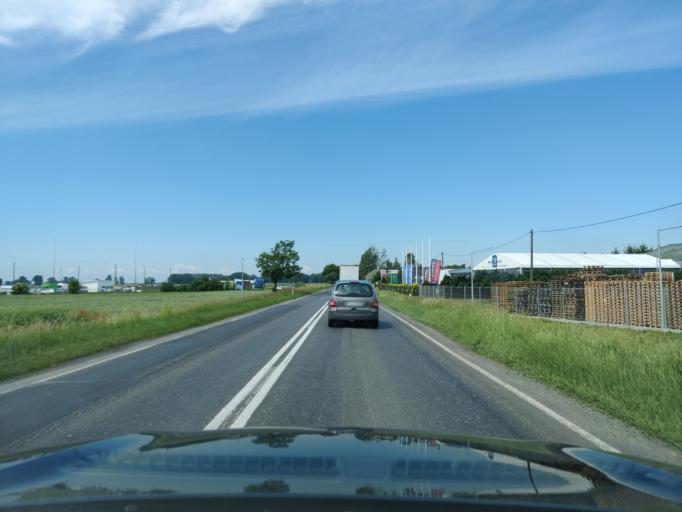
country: PL
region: Greater Poland Voivodeship
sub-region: Powiat grodziski
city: Granowo
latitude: 52.2230
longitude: 16.5141
